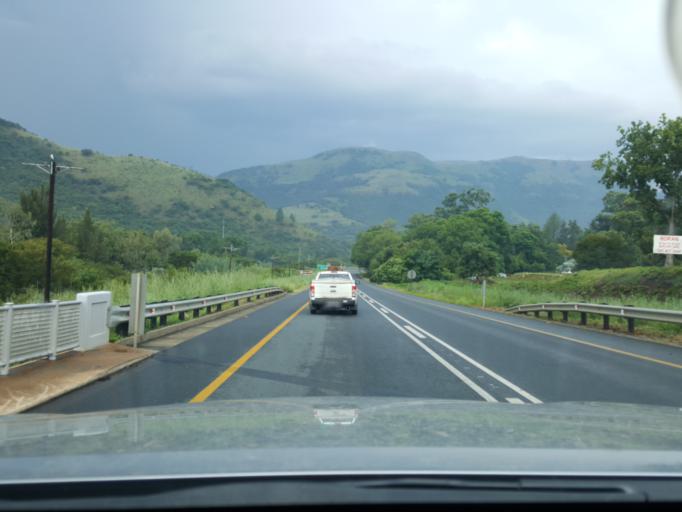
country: ZA
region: Mpumalanga
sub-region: Nkangala District Municipality
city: Belfast
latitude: -25.6473
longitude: 30.3804
